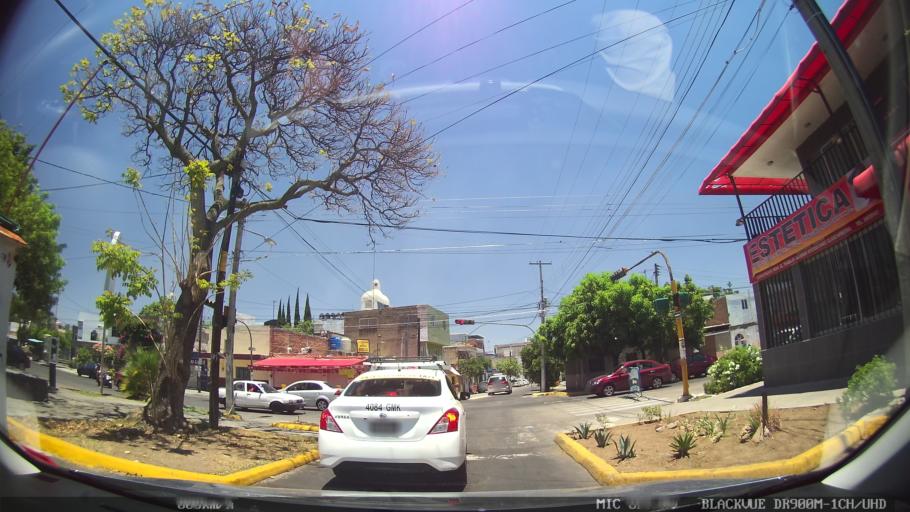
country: MX
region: Jalisco
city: Tlaquepaque
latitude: 20.6740
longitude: -103.2861
